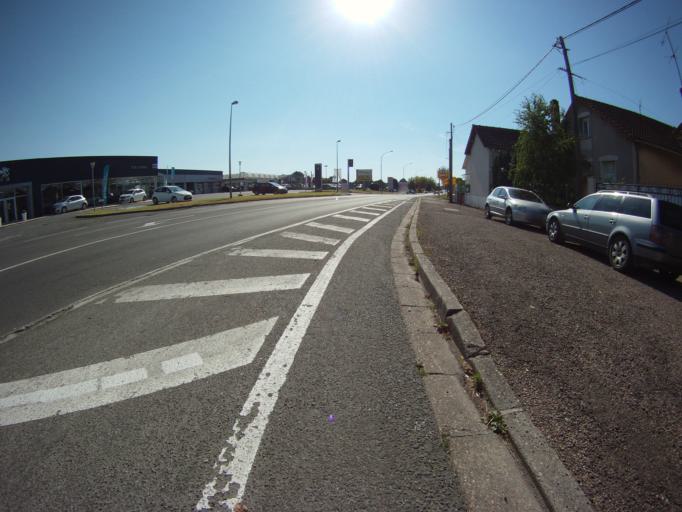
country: FR
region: Bourgogne
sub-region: Departement de la Nievre
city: Varennes-Vauzelles
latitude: 46.9961
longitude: 3.1293
